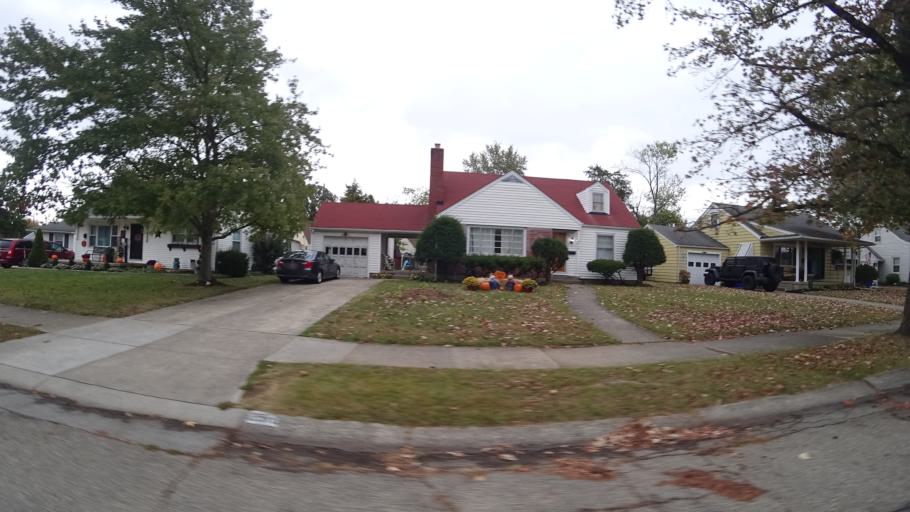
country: US
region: Ohio
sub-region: Butler County
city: Fairfield
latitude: 39.3623
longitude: -84.5606
